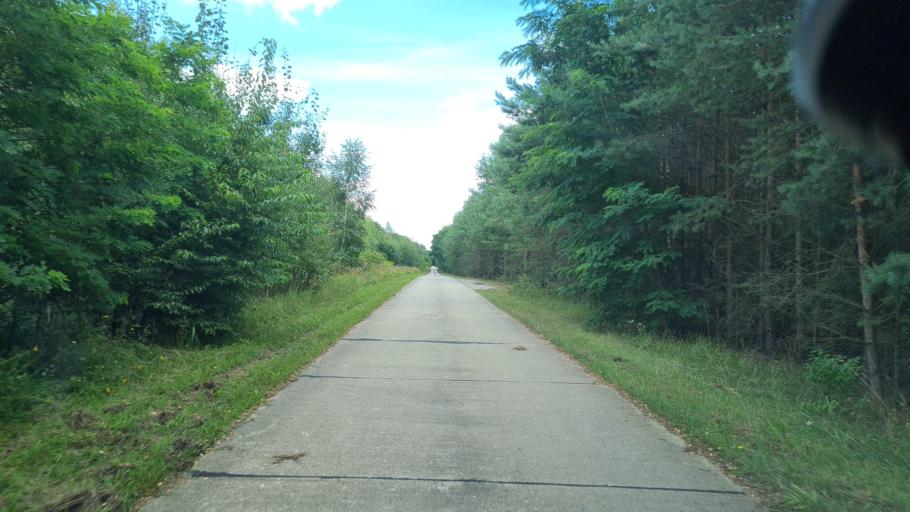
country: DE
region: Brandenburg
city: Drebkau
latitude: 51.6197
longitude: 14.2715
